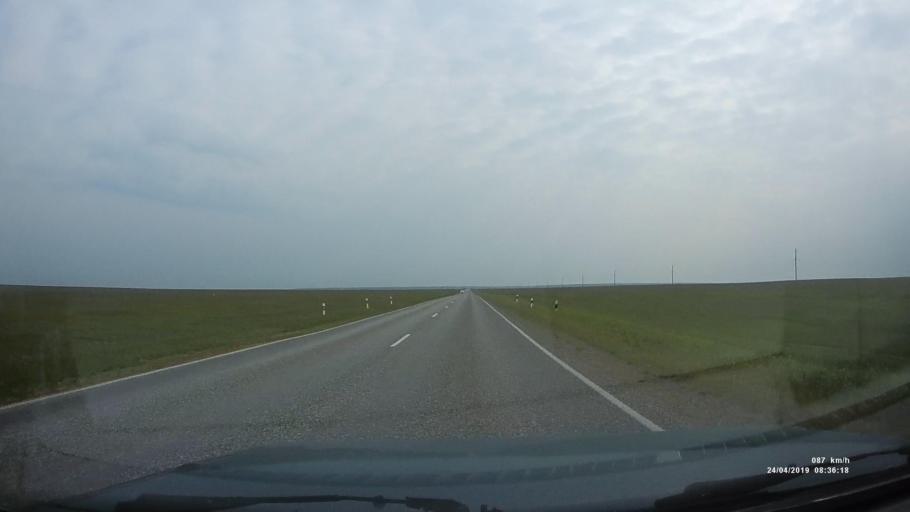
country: RU
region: Kalmykiya
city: Arshan'
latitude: 46.2038
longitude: 43.9320
